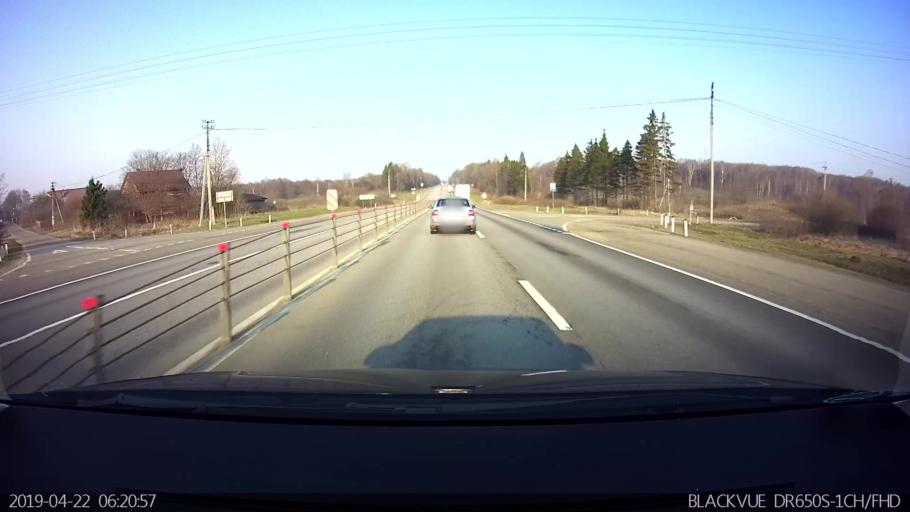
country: RU
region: Moskovskaya
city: Mozhaysk
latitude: 55.4652
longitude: 35.8880
